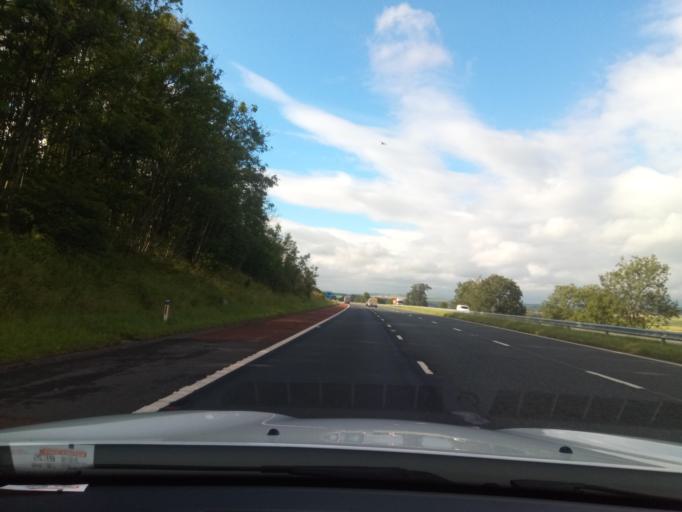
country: GB
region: England
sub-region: Cumbria
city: Penrith
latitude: 54.7002
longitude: -2.7914
